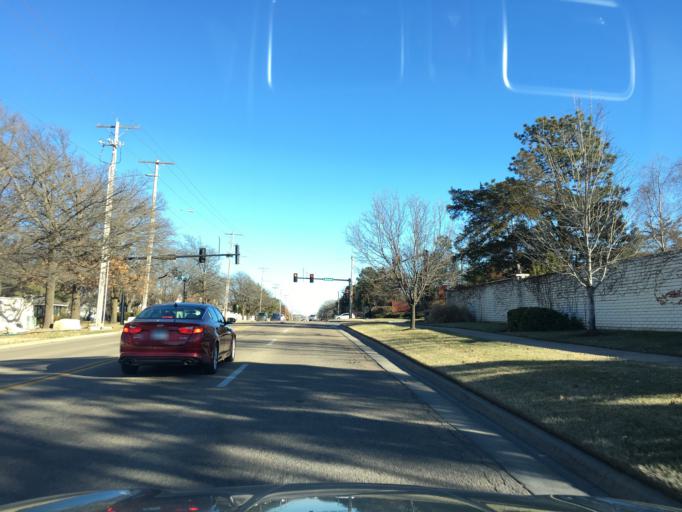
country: US
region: Kansas
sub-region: Sedgwick County
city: Bellaire
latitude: 37.7084
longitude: -97.2339
